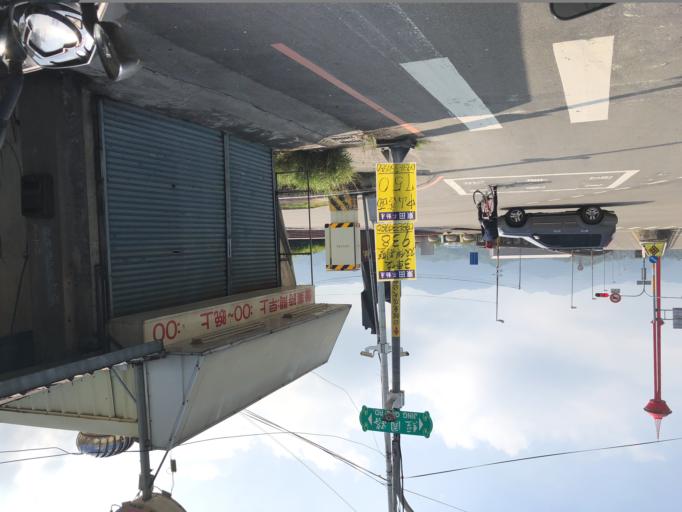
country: TW
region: Taiwan
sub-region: Miaoli
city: Miaoli
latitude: 24.5468
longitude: 120.8276
